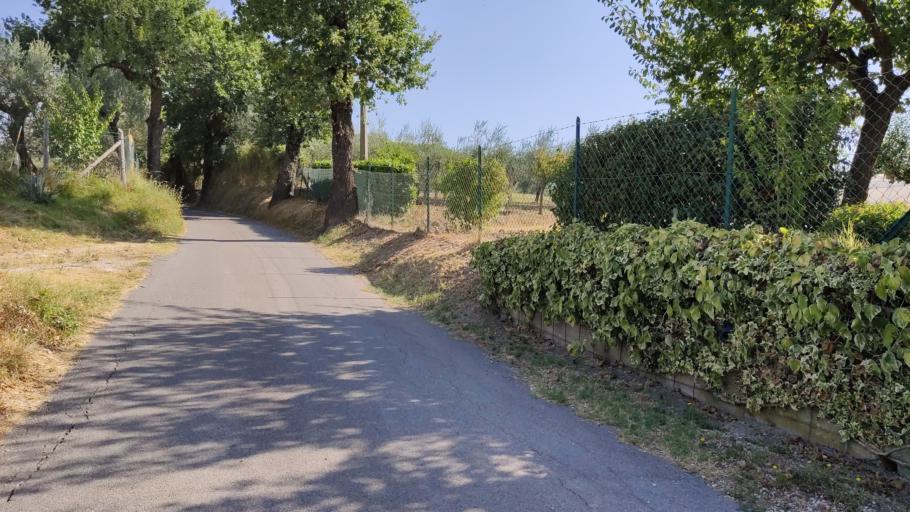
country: IT
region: Umbria
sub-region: Provincia di Terni
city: Amelia
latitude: 42.5346
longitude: 12.4105
